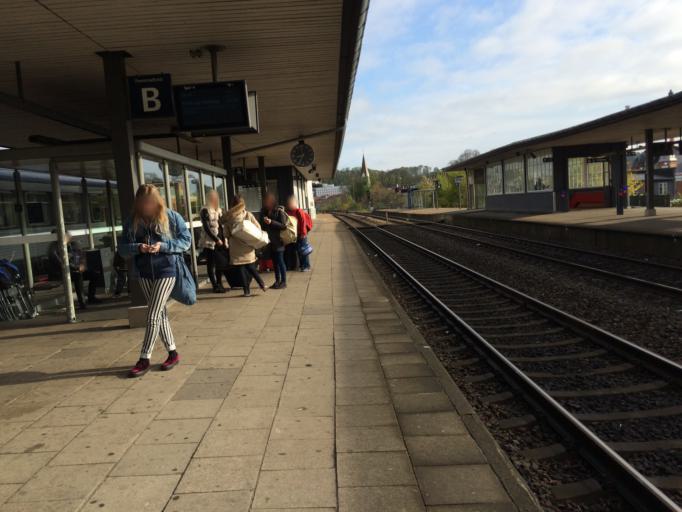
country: DK
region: South Denmark
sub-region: Vejle Kommune
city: Vejle
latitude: 55.7062
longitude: 9.5370
